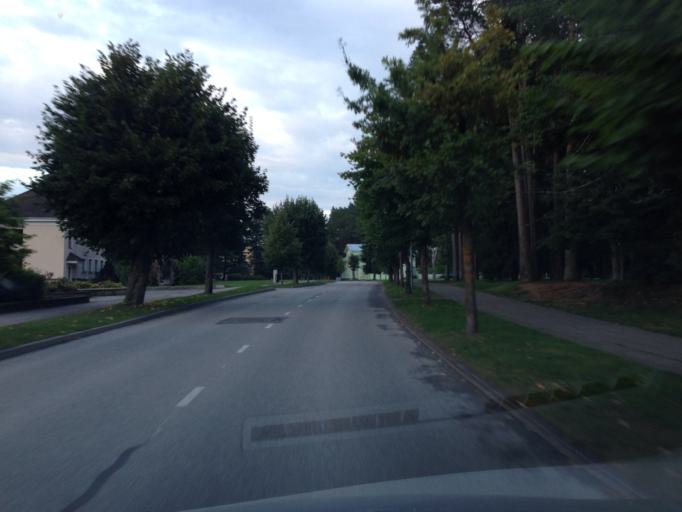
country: EE
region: Tartu
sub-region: Elva linn
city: Elva
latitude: 58.2232
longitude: 26.4162
